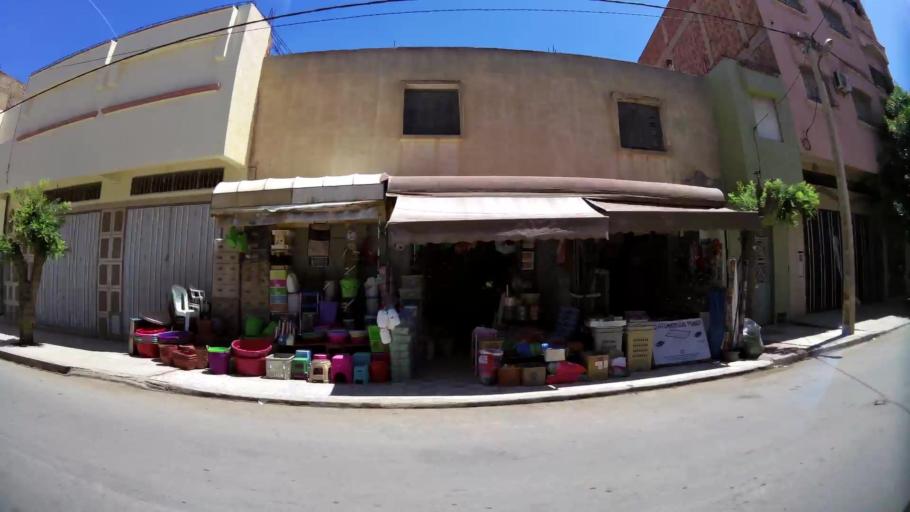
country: MA
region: Oriental
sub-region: Oujda-Angad
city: Oujda
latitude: 34.6670
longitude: -1.9364
